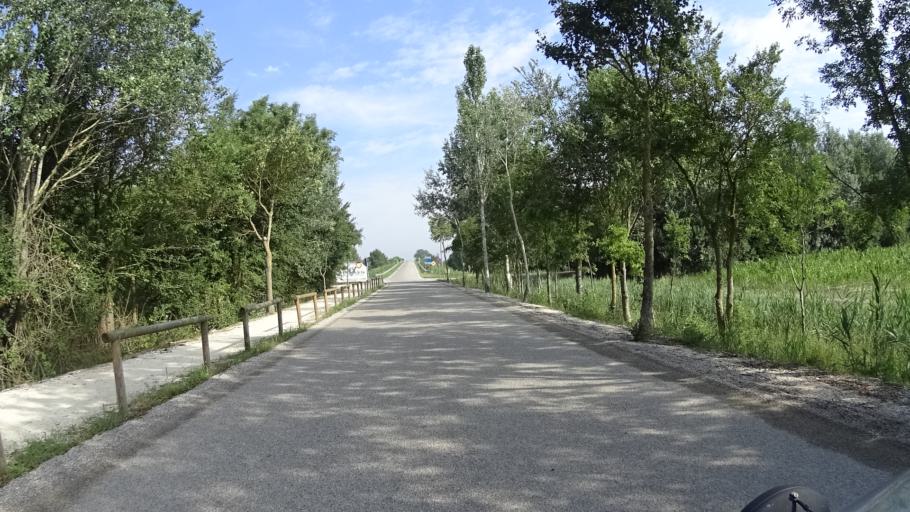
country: IT
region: Veneto
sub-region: Provincia di Venezia
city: Caorle
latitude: 45.6356
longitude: 12.9507
